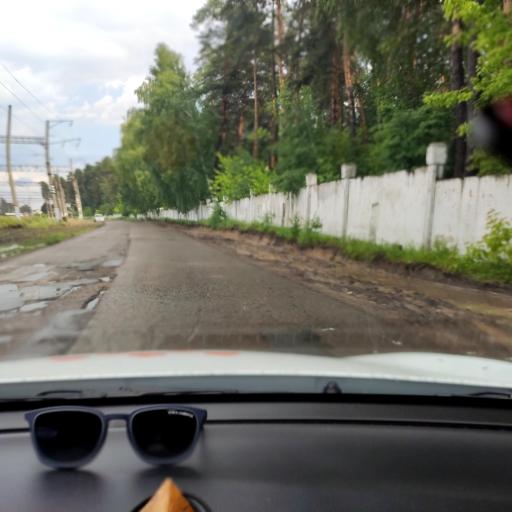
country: RU
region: Tatarstan
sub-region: Zelenodol'skiy Rayon
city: Vasil'yevo
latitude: 55.8369
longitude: 48.6956
